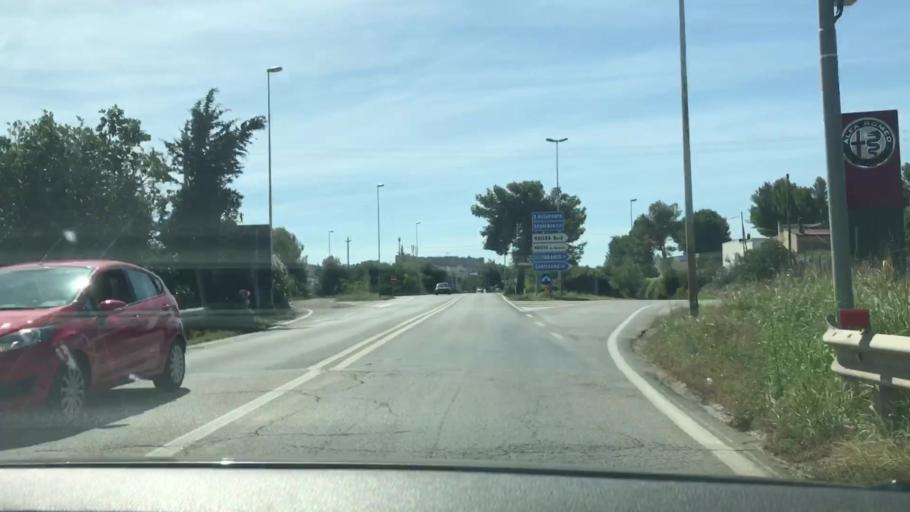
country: IT
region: Basilicate
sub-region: Provincia di Matera
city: Matera
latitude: 40.6862
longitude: 16.5902
